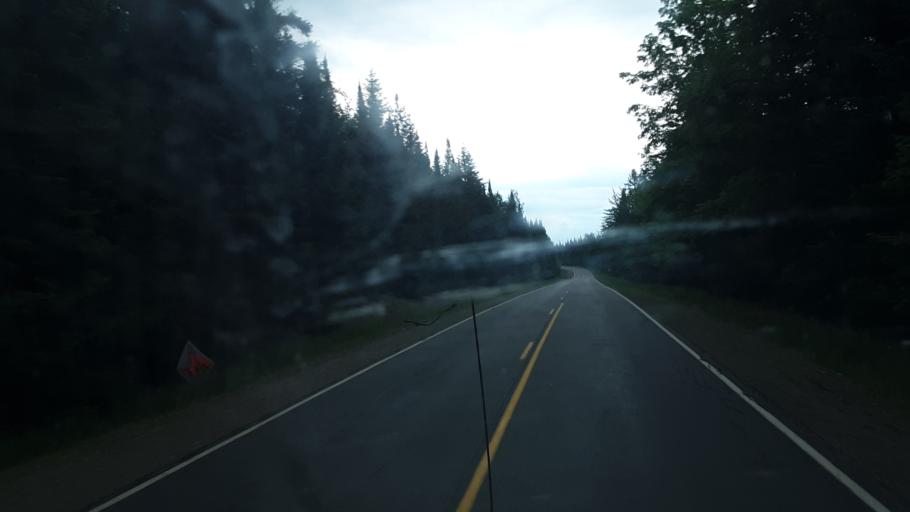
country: US
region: Maine
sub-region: Penobscot County
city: Medway
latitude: 45.7007
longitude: -68.2916
